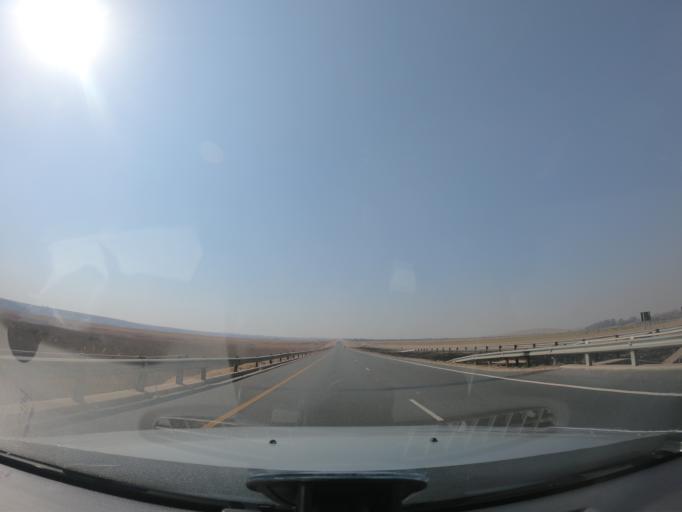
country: ZA
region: Mpumalanga
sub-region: Nkangala District Municipality
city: Witbank
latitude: -25.8696
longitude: 29.0101
